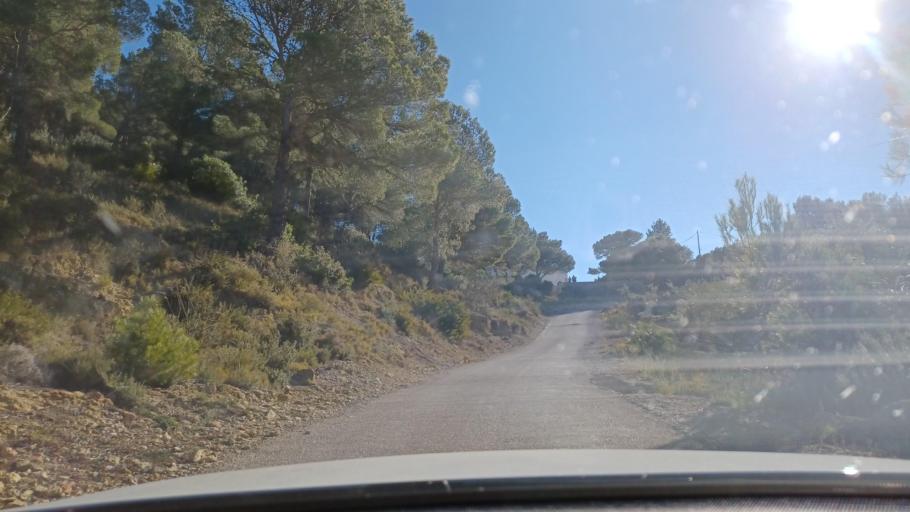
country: ES
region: Catalonia
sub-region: Provincia de Tarragona
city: Tortosa
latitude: 40.8168
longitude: 0.5699
